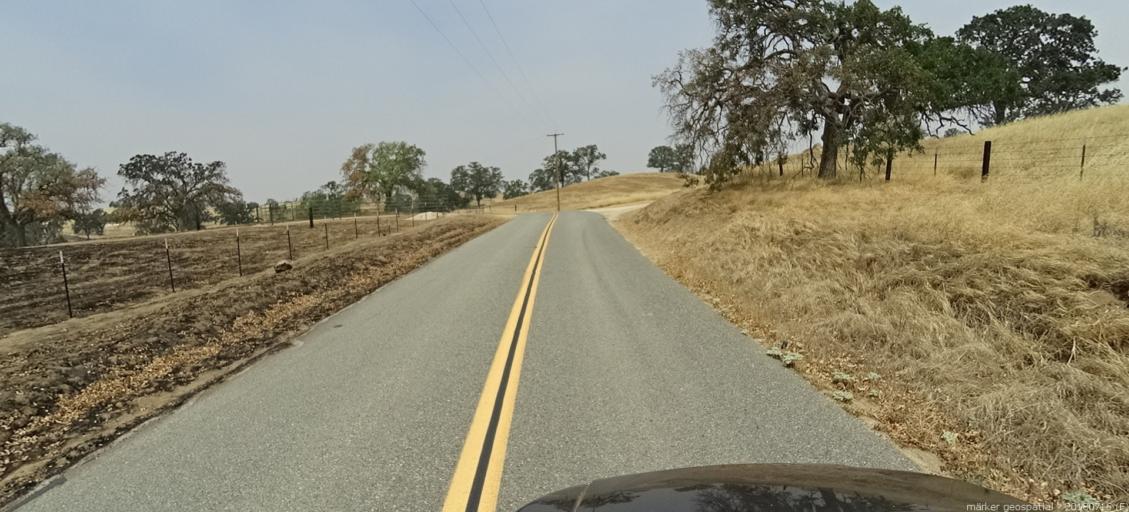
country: US
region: California
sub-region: Madera County
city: Yosemite Lakes
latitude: 37.1468
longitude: -119.9094
